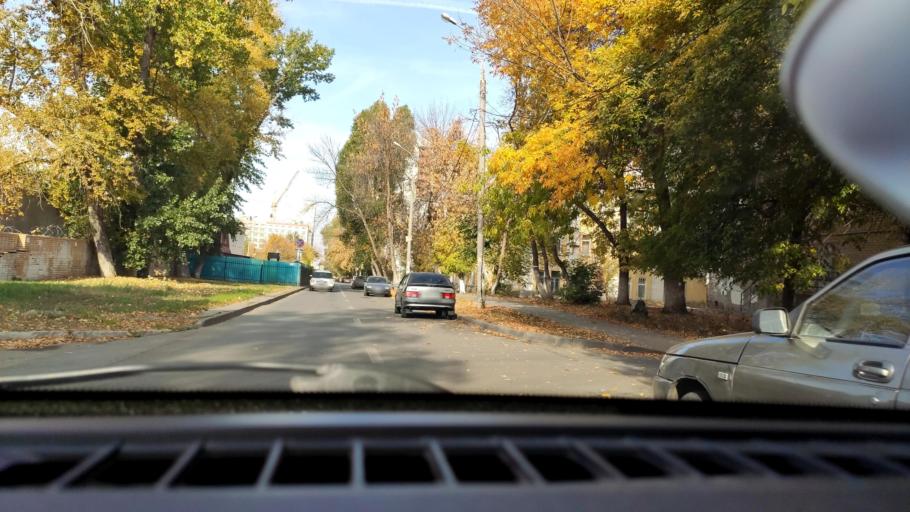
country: RU
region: Samara
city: Samara
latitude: 53.2075
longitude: 50.1651
